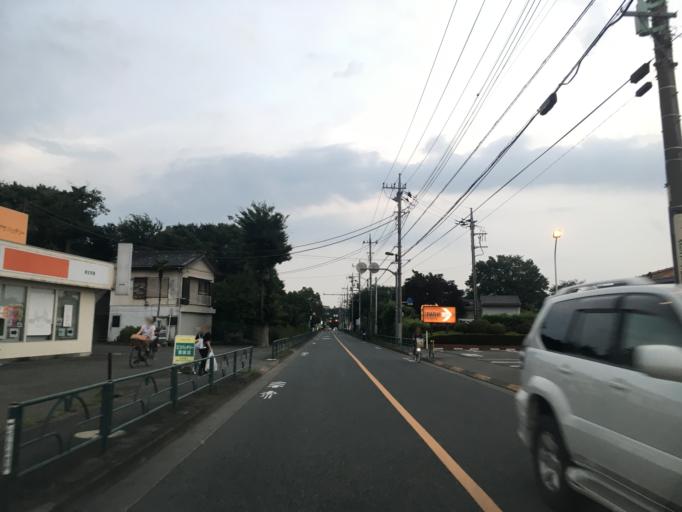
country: JP
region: Tokyo
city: Kokubunji
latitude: 35.7176
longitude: 139.4689
